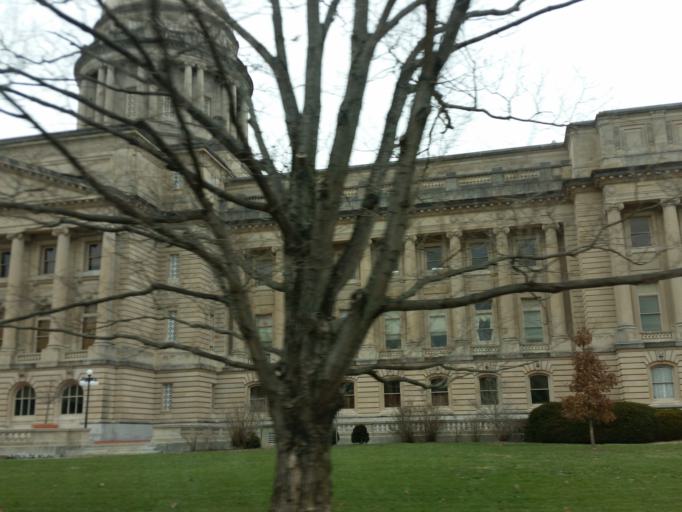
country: US
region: Kentucky
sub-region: Franklin County
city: Frankfort
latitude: 38.1861
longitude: -84.8751
